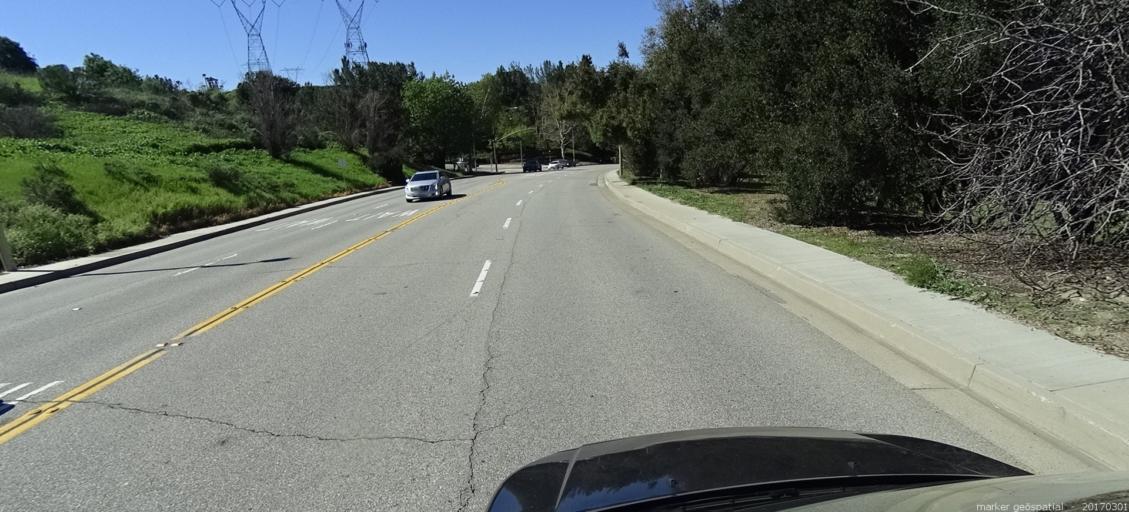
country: US
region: California
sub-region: Orange County
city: Villa Park
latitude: 33.8412
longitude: -117.7724
